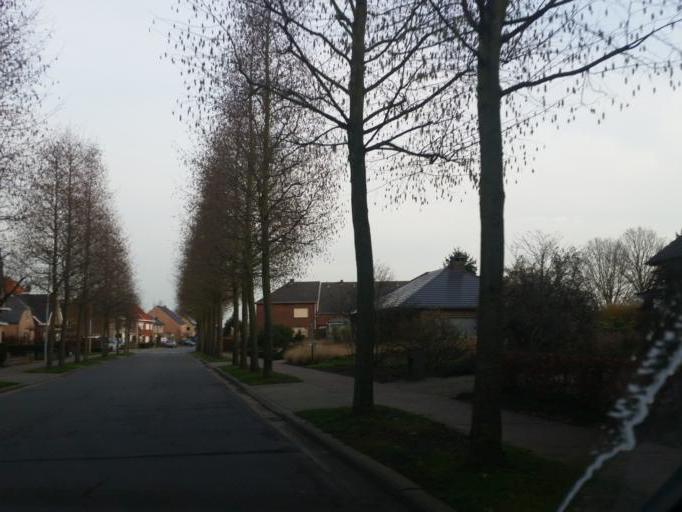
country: BE
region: Flanders
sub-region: Provincie Antwerpen
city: Duffel
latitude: 51.0705
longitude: 4.5046
